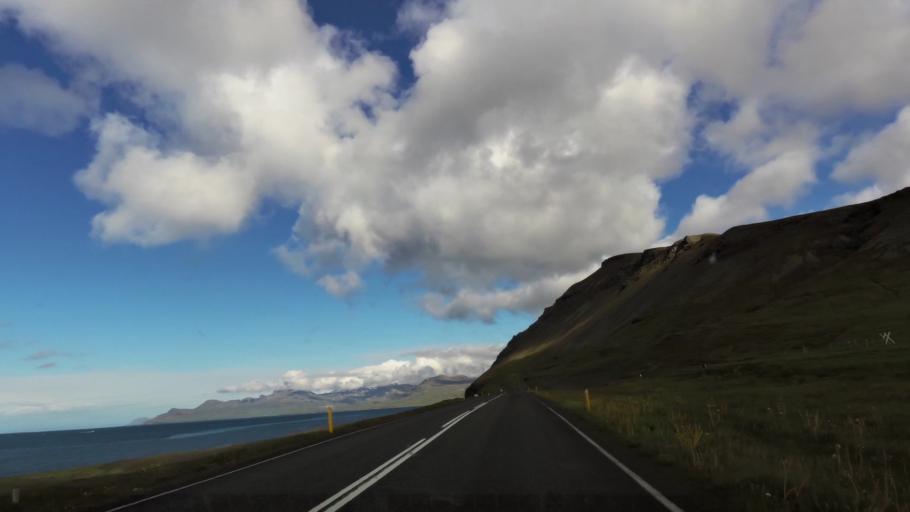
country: IS
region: West
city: Olafsvik
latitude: 64.9033
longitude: -23.7772
